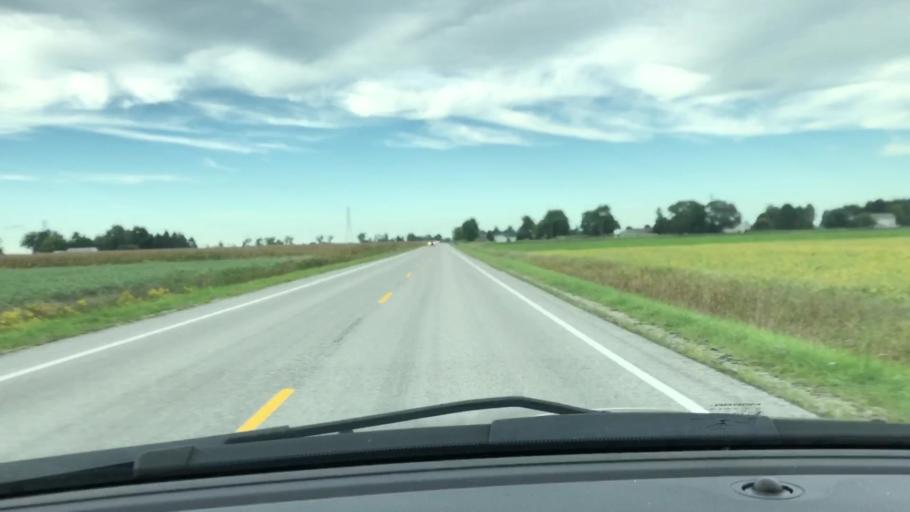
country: US
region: Michigan
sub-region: Bay County
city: Auburn
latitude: 43.5479
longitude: -84.0332
